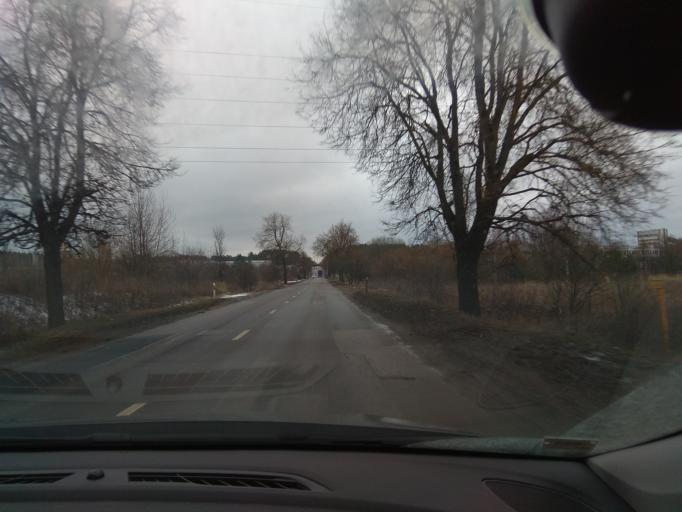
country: LT
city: Grigiskes
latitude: 54.6468
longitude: 25.1315
